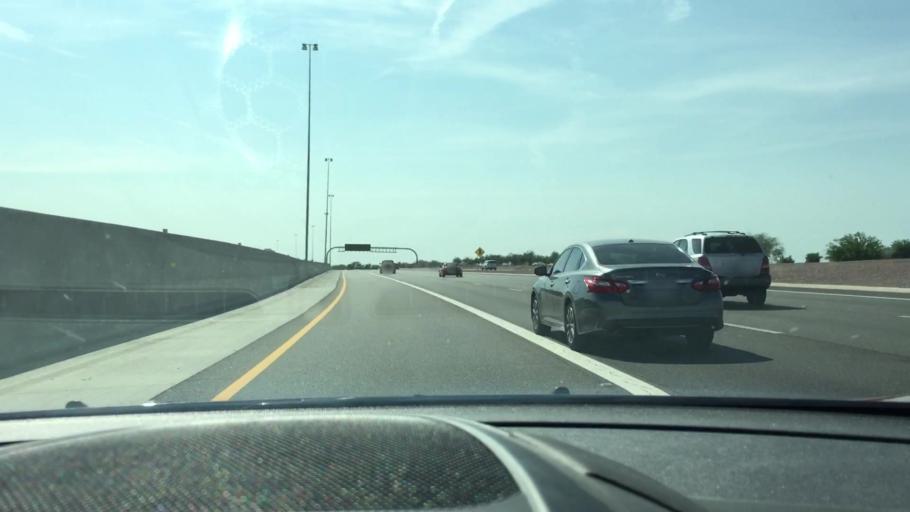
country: US
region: Arizona
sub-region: Maricopa County
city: Mesa
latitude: 33.4908
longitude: -111.7522
